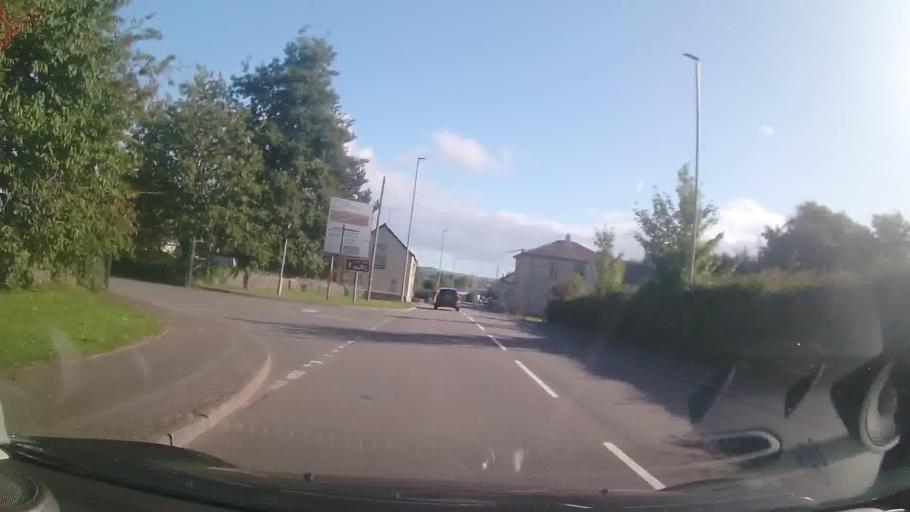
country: GB
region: Wales
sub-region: Carmarthenshire
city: Saint Clears
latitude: 51.8182
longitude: -4.5027
